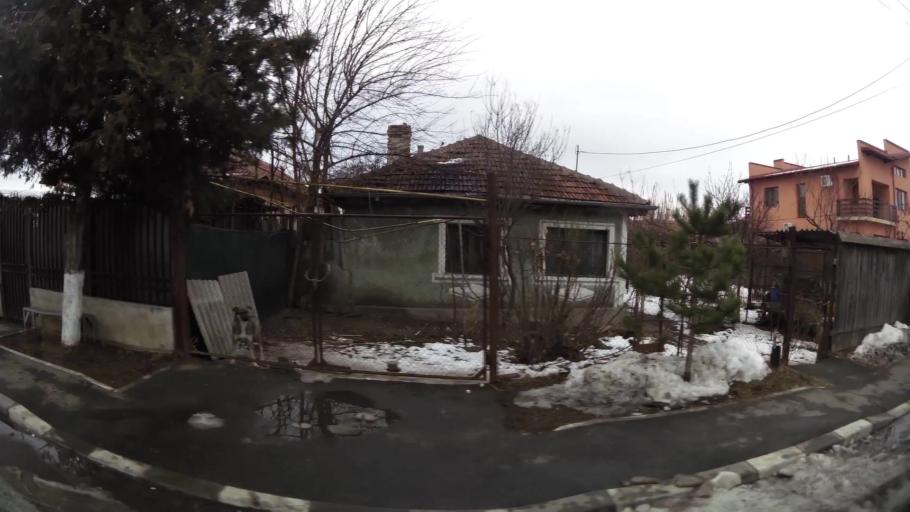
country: RO
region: Ilfov
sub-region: Voluntari City
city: Voluntari
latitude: 44.4980
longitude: 26.1996
